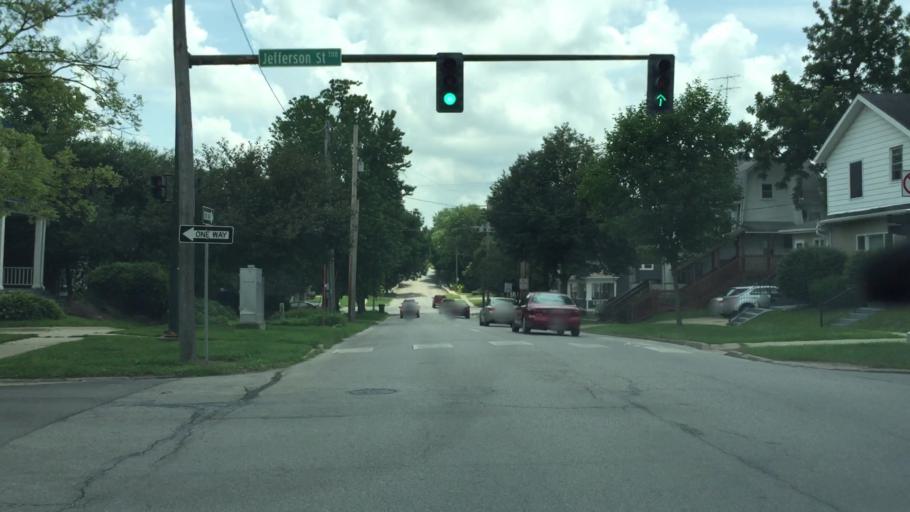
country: US
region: Iowa
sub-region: Johnson County
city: Iowa City
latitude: 41.6625
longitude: -91.5258
